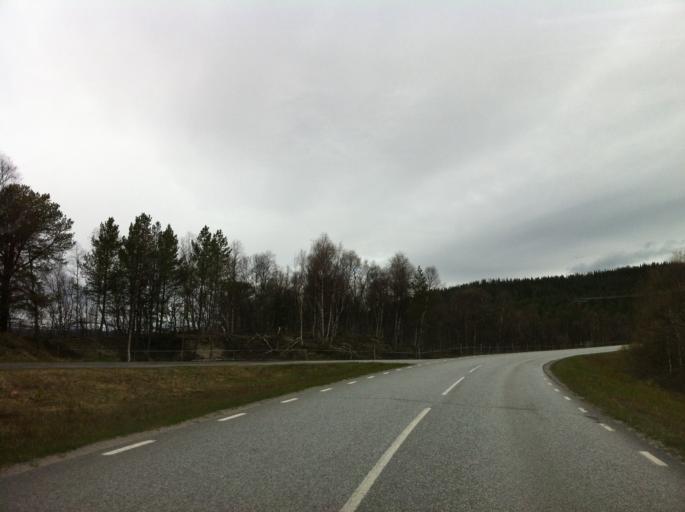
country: NO
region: Sor-Trondelag
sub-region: Tydal
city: Aas
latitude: 62.6039
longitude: 12.5123
